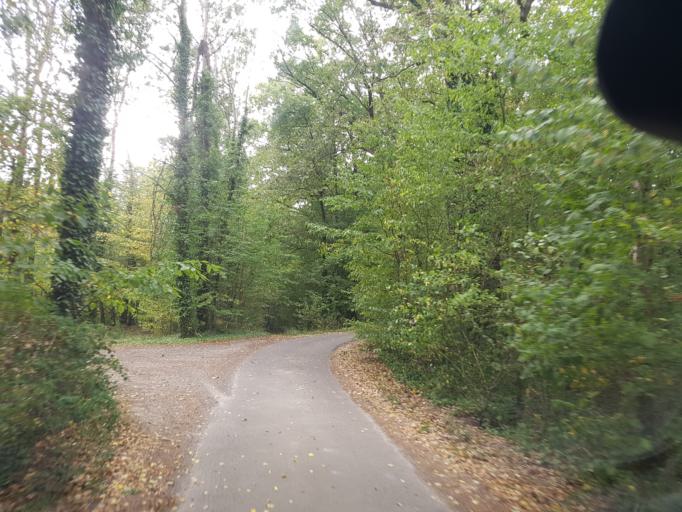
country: DE
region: Brandenburg
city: Calau
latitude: 51.7186
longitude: 13.9327
